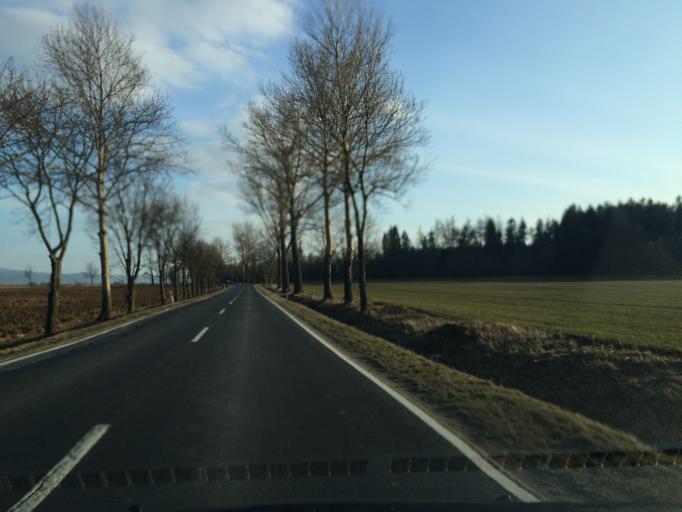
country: PL
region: Lower Silesian Voivodeship
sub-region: Powiat klodzki
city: Bystrzyca Klodzka
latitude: 50.2404
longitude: 16.6736
